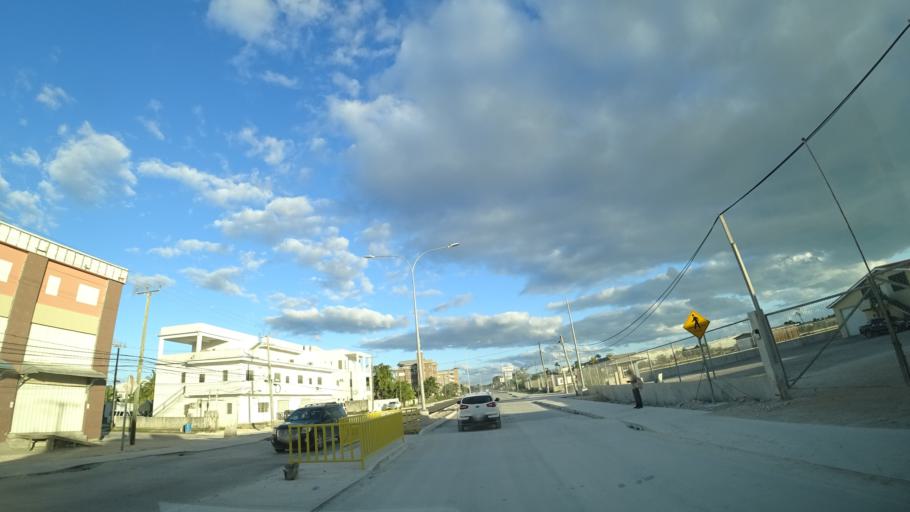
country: BZ
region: Belize
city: Belize City
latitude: 17.5161
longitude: -88.2275
